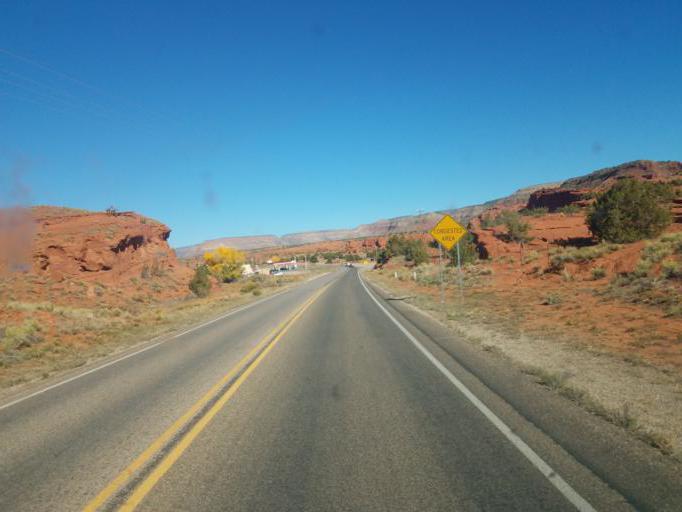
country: US
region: New Mexico
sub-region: Sandoval County
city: Jemez Pueblo
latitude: 35.6405
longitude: -106.7247
